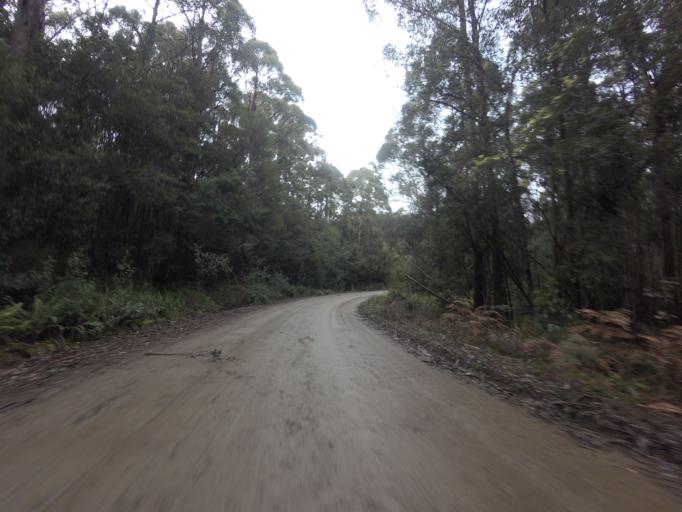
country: AU
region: Tasmania
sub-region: Huon Valley
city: Geeveston
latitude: -43.4986
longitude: 146.8790
